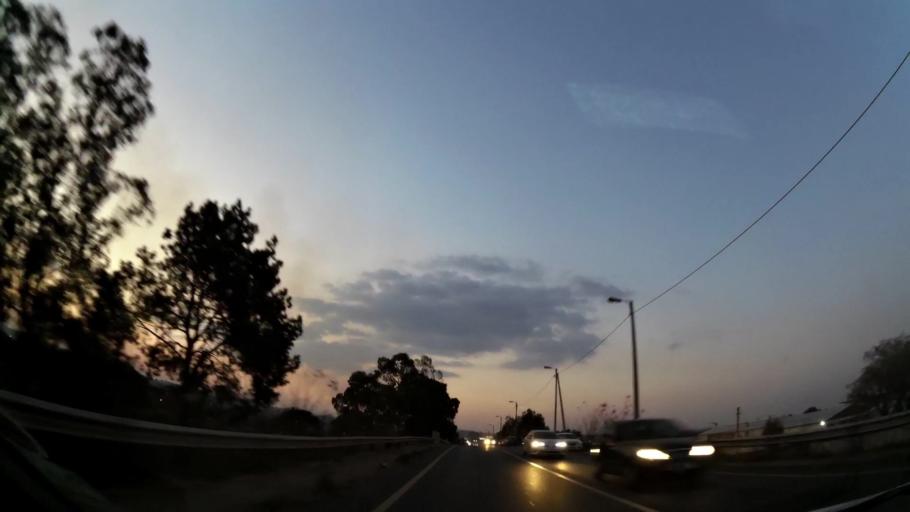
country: ZA
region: Gauteng
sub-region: Ekurhuleni Metropolitan Municipality
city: Springs
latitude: -26.2860
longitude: 28.4534
